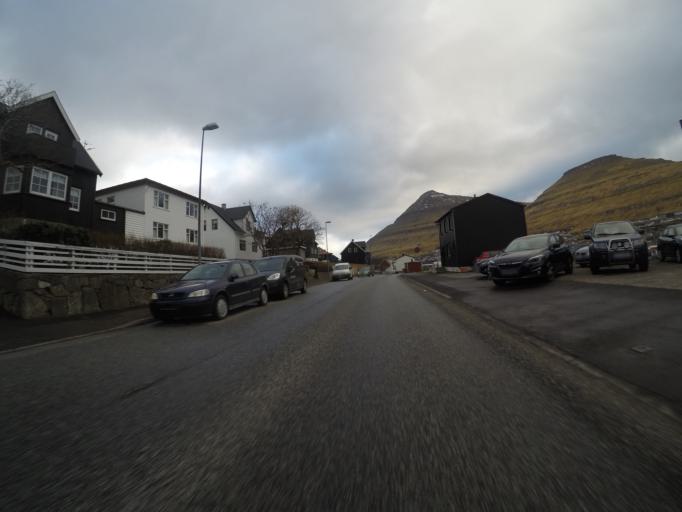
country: FO
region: Nordoyar
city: Klaksvik
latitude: 62.2337
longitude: -6.5906
